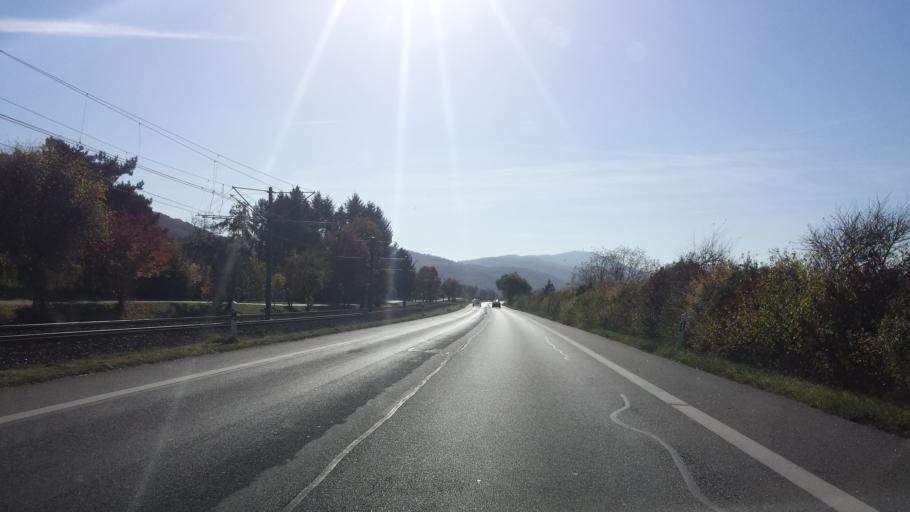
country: DE
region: Hesse
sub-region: Regierungsbezirk Darmstadt
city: Seeheim-Jugenheim
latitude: 49.7862
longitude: 8.6486
